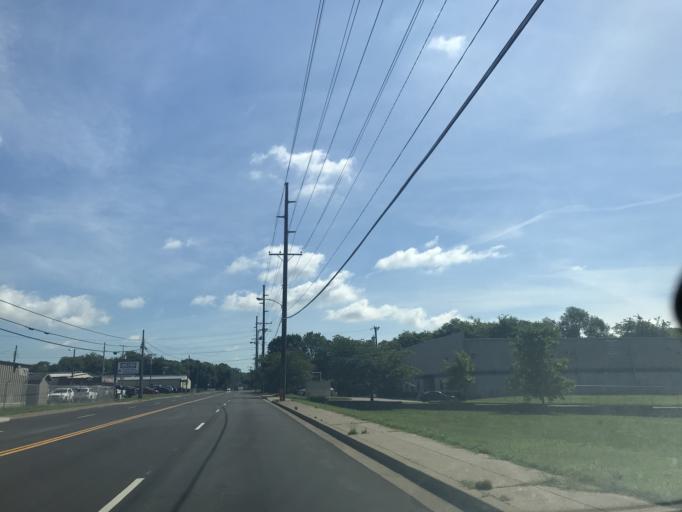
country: US
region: Tennessee
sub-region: Davidson County
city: Nashville
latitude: 36.1877
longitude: -86.8395
